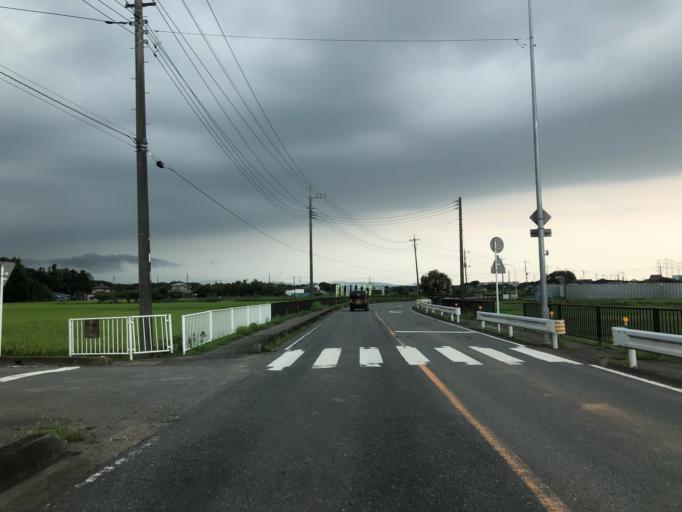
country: JP
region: Saitama
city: Sakado
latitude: 36.0188
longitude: 139.4018
